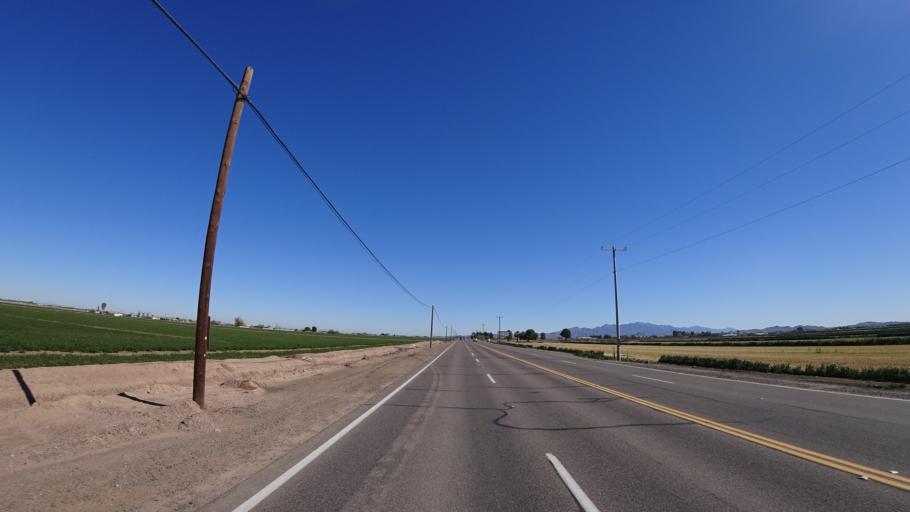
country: US
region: Arizona
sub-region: Maricopa County
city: Buckeye
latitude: 33.3777
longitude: -112.5318
